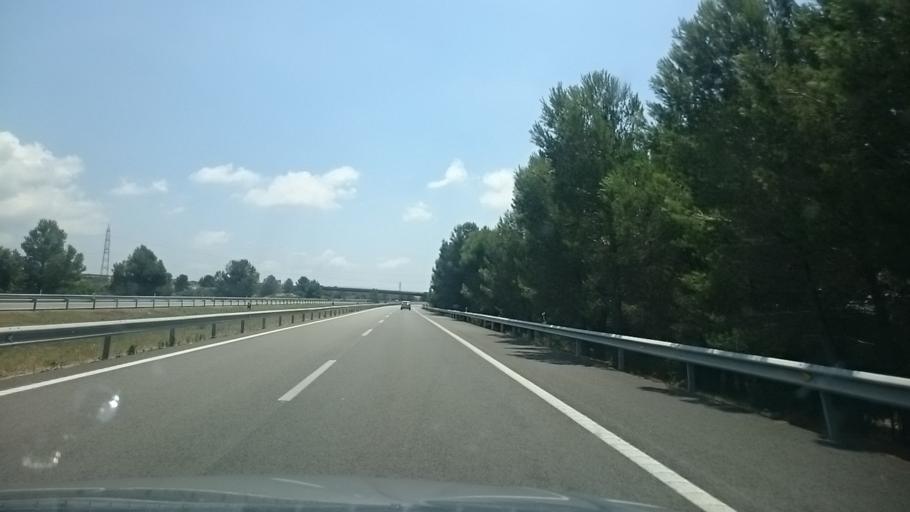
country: ES
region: Catalonia
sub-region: Provincia de Tarragona
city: Alio
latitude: 41.3209
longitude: 1.3296
